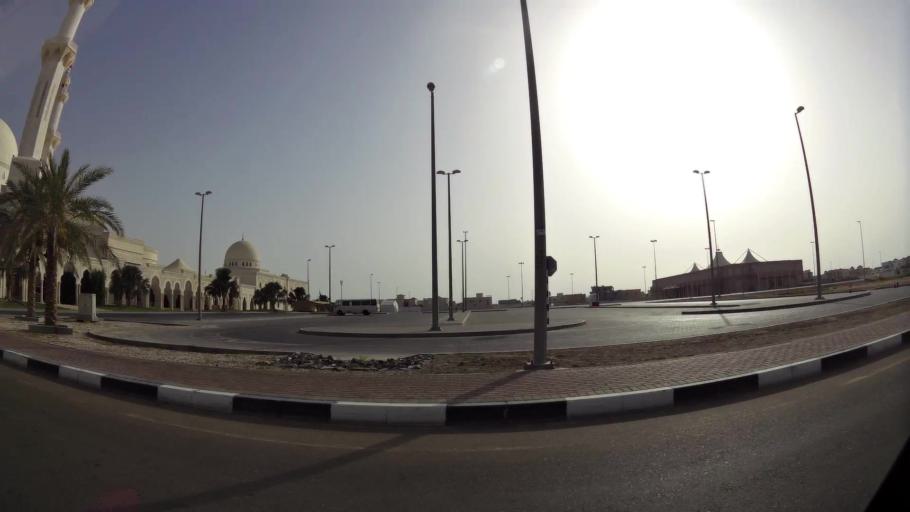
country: AE
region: Abu Dhabi
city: Al Ain
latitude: 24.1276
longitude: 55.6865
